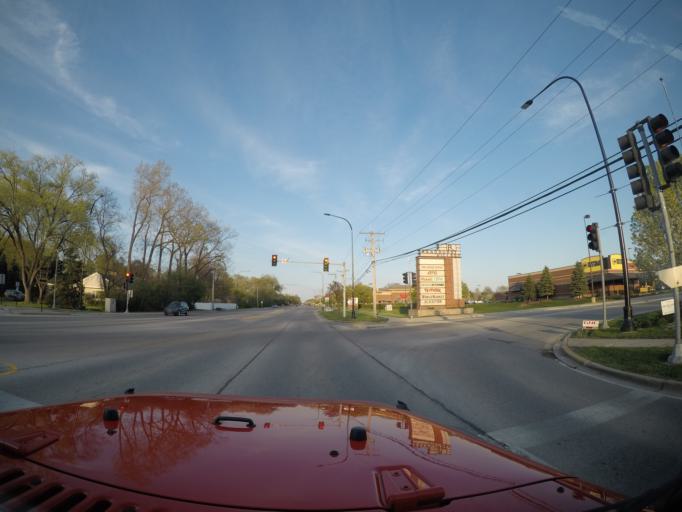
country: US
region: Illinois
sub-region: Cook County
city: Prospect Heights
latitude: 42.0880
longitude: -87.9335
